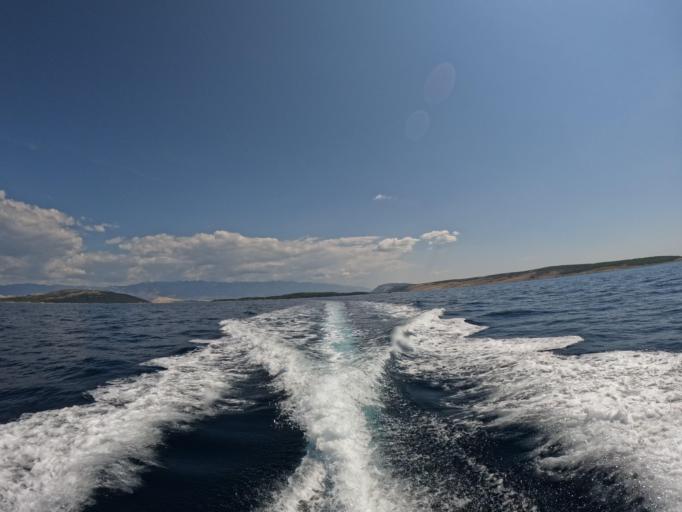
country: HR
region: Primorsko-Goranska
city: Lopar
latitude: 44.8627
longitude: 14.6909
